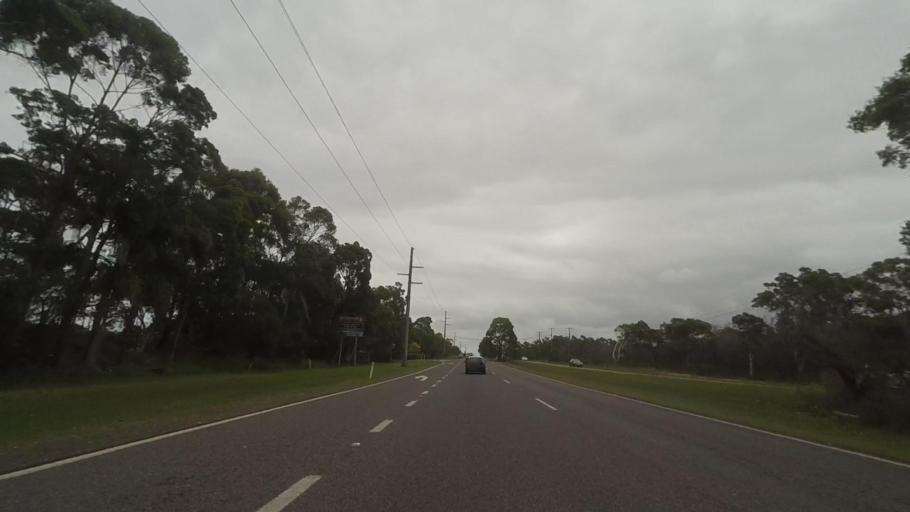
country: AU
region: New South Wales
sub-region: Wyong Shire
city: Kingfisher Shores
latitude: -33.1873
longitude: 151.5829
